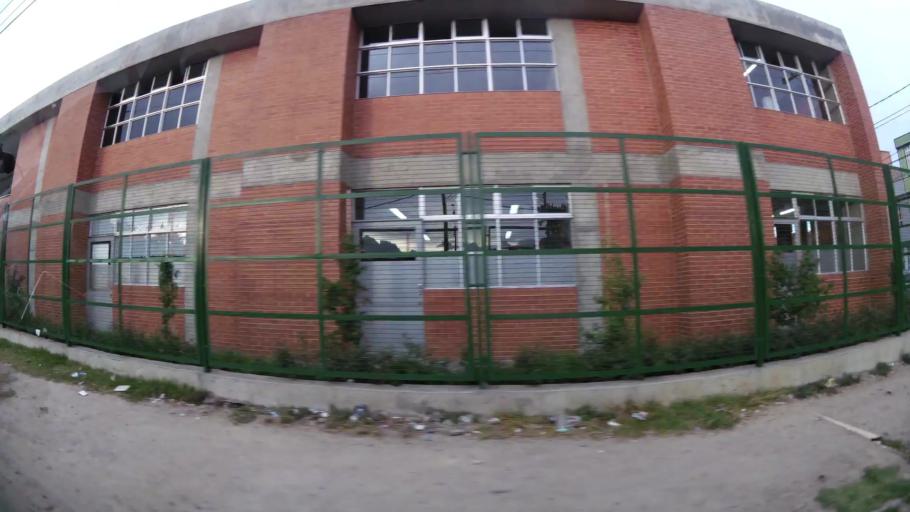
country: CO
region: Cundinamarca
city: Soacha
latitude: 4.6216
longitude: -74.1613
